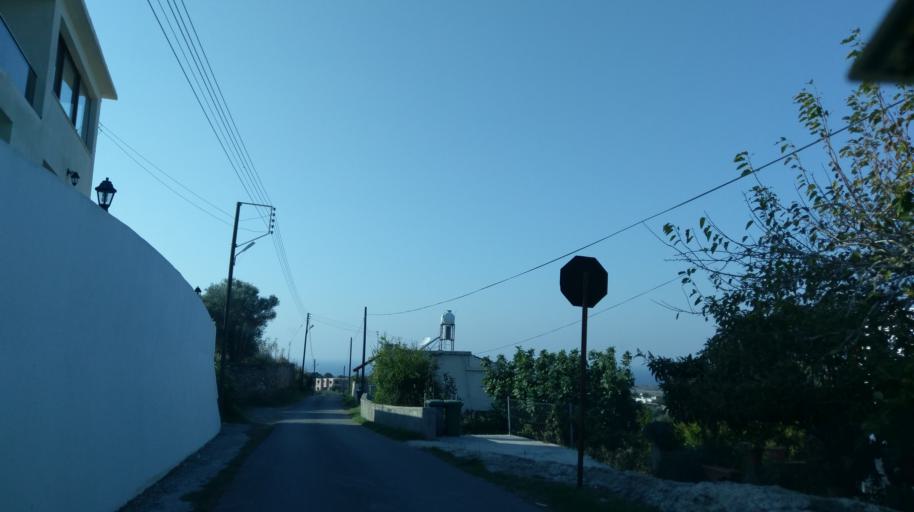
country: CY
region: Ammochostos
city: Leonarisso
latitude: 35.5376
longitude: 34.1911
